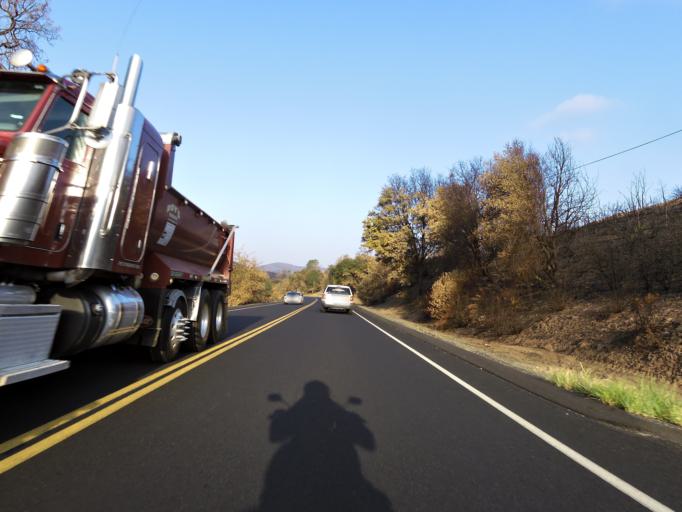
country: US
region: California
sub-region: Mariposa County
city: Mariposa
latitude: 37.5147
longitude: -120.0613
